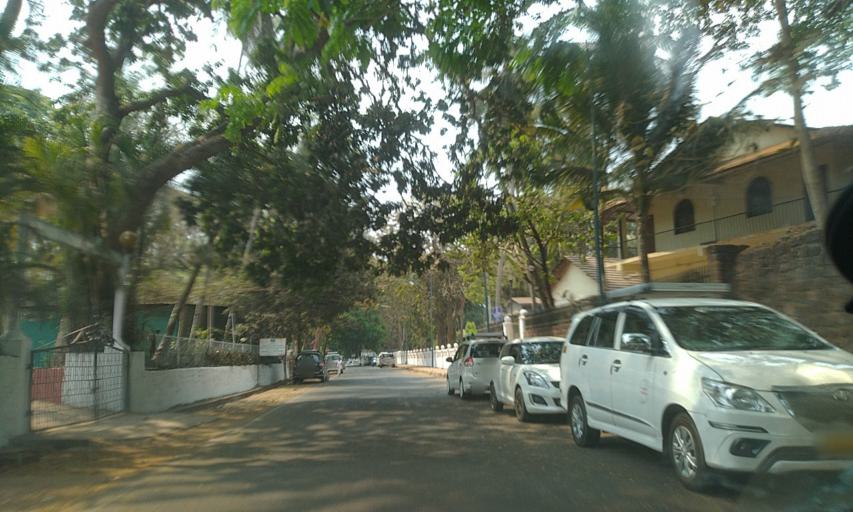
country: IN
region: Goa
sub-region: North Goa
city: Jua
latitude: 15.5032
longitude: 73.9136
